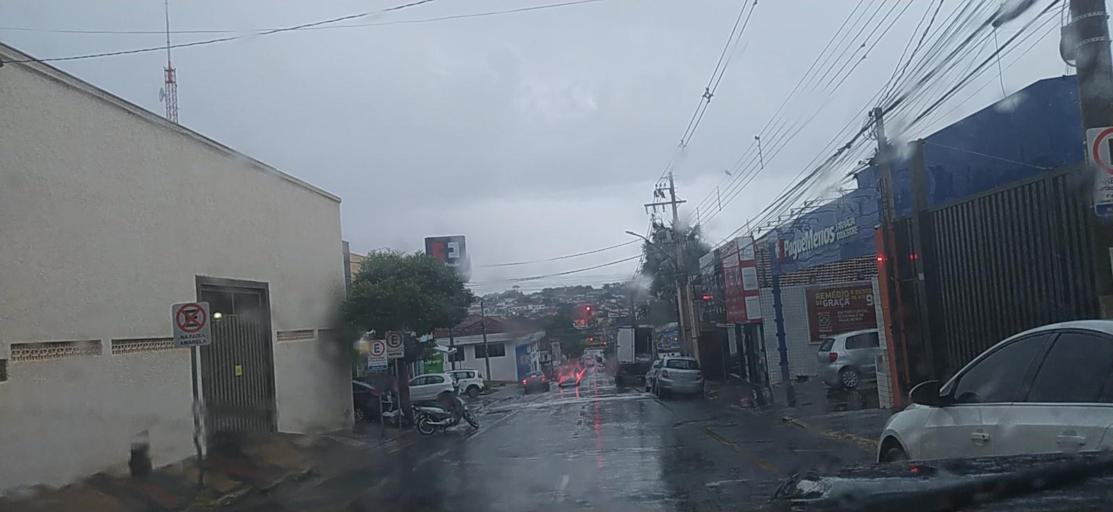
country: BR
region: Sao Paulo
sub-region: Catanduva
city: Catanduva
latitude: -21.1363
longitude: -48.9705
